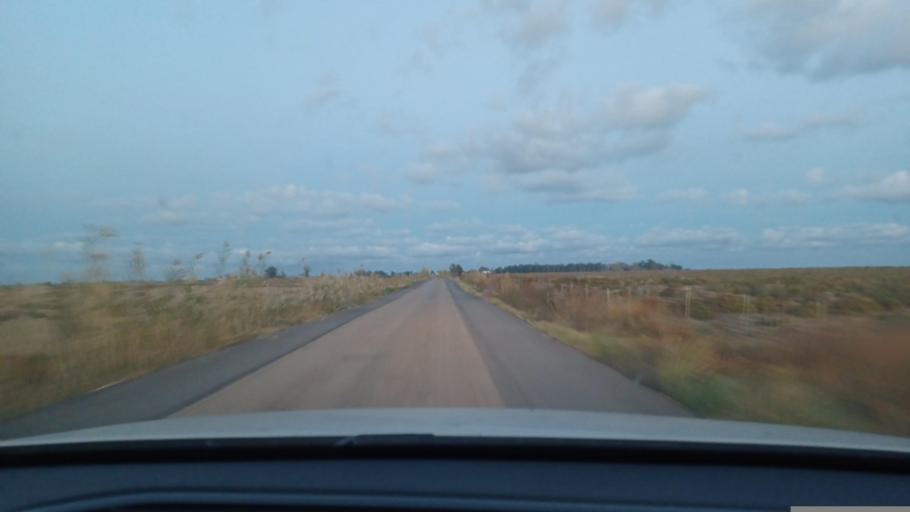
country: ES
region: Catalonia
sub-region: Provincia de Tarragona
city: Deltebre
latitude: 40.6519
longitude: 0.7649
